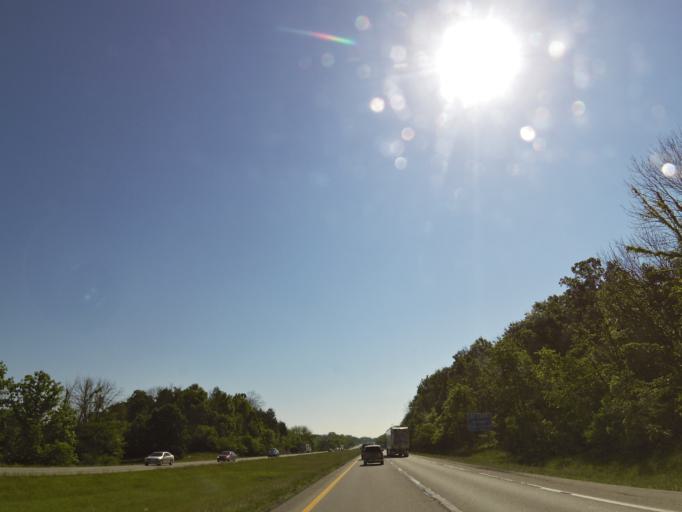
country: US
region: Kentucky
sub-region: Franklin County
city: Frankfort
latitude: 38.1555
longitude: -84.9286
